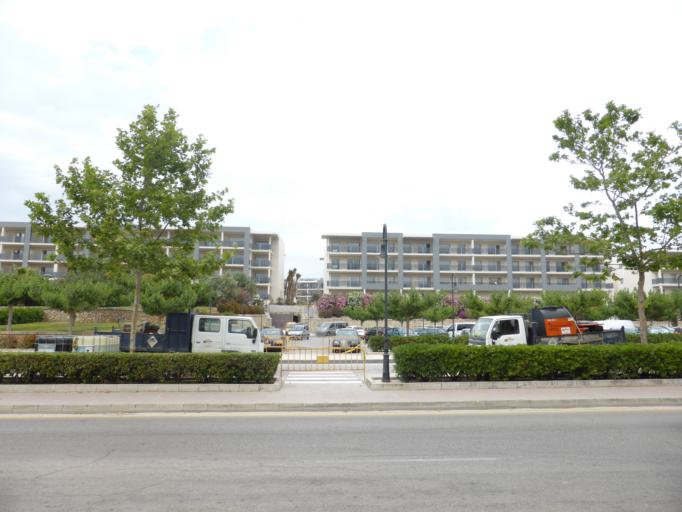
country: ES
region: Balearic Islands
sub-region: Illes Balears
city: Port d'Alcudia
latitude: 39.8437
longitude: 3.1335
